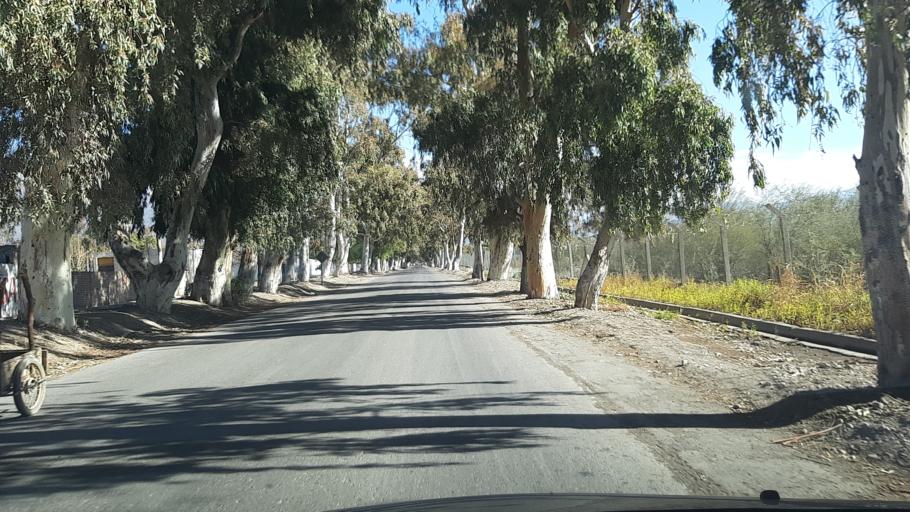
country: AR
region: San Juan
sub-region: Departamento de Zonda
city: Zonda
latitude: -31.5460
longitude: -68.7258
